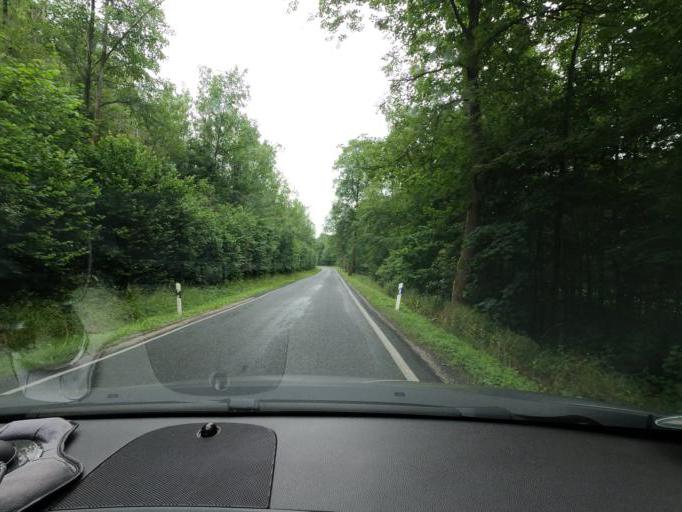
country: DE
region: Thuringia
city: Heilbad Heiligenstadt
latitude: 51.3518
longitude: 10.1617
